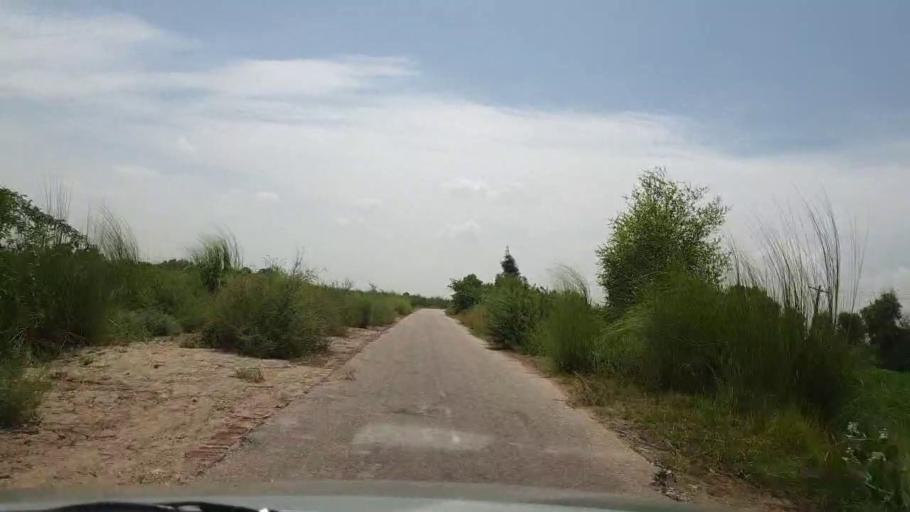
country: PK
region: Sindh
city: Bozdar
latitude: 27.0677
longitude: 68.9811
